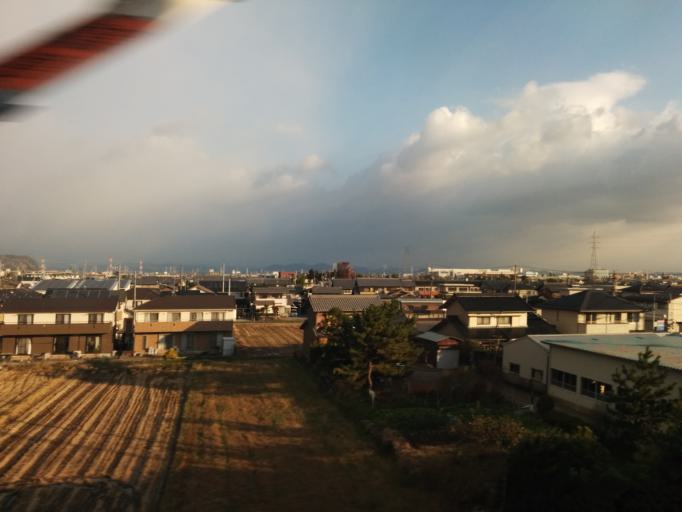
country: JP
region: Gifu
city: Ogaki
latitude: 35.3486
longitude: 136.5926
